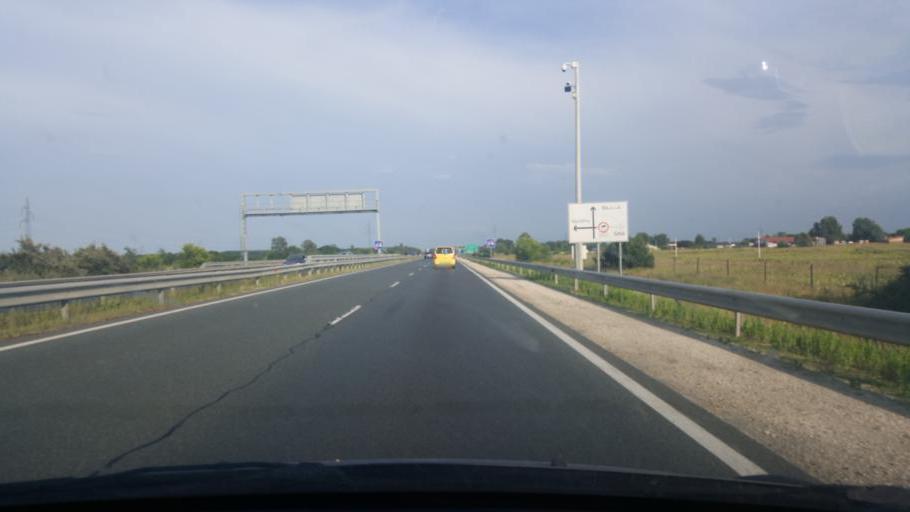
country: HU
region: Pest
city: Ullo
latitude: 47.3985
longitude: 19.3592
